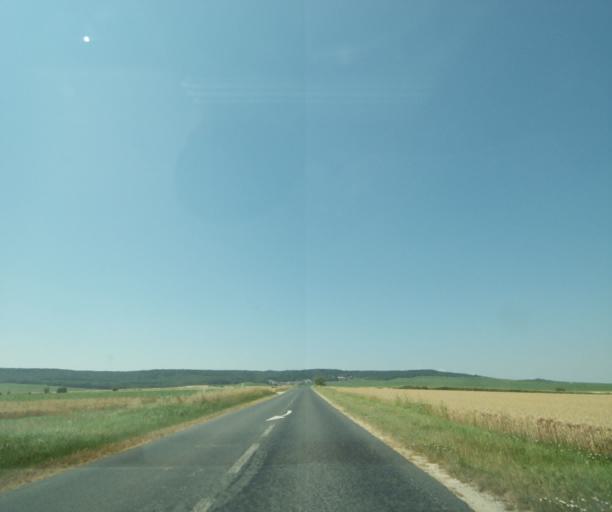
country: FR
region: Champagne-Ardenne
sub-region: Departement de la Marne
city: Verzy
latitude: 49.1592
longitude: 4.1996
